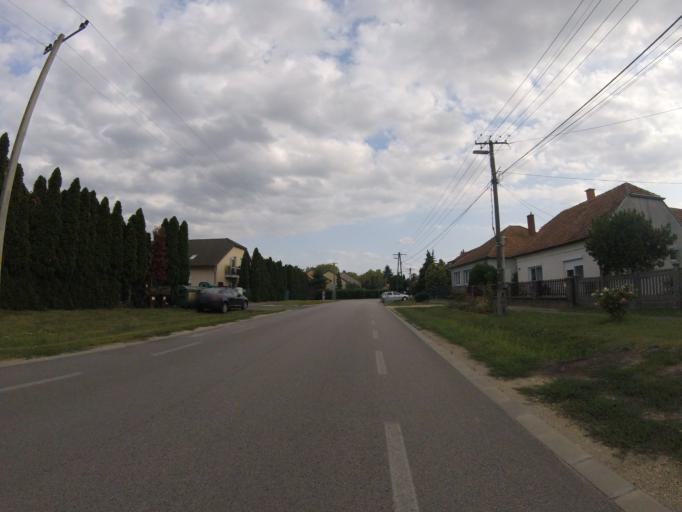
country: HU
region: Gyor-Moson-Sopron
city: Fertod
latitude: 47.6235
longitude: 16.8652
